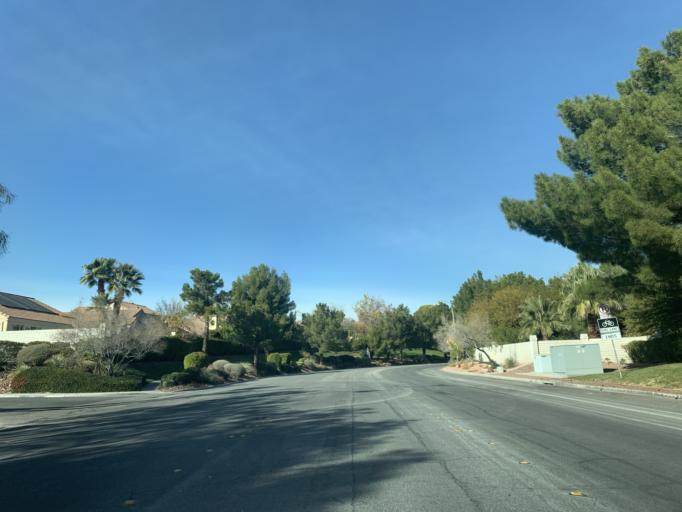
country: US
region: Nevada
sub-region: Clark County
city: Summerlin South
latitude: 36.1315
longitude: -115.2898
